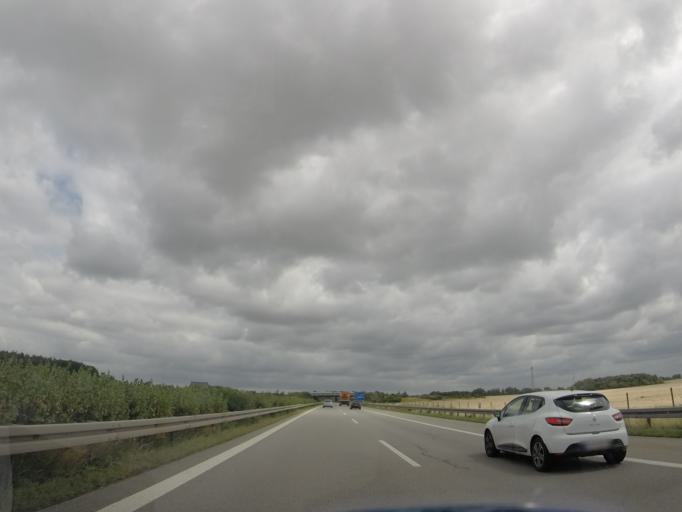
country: DE
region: Mecklenburg-Vorpommern
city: Ziesendorf
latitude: 54.0149
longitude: 12.0468
